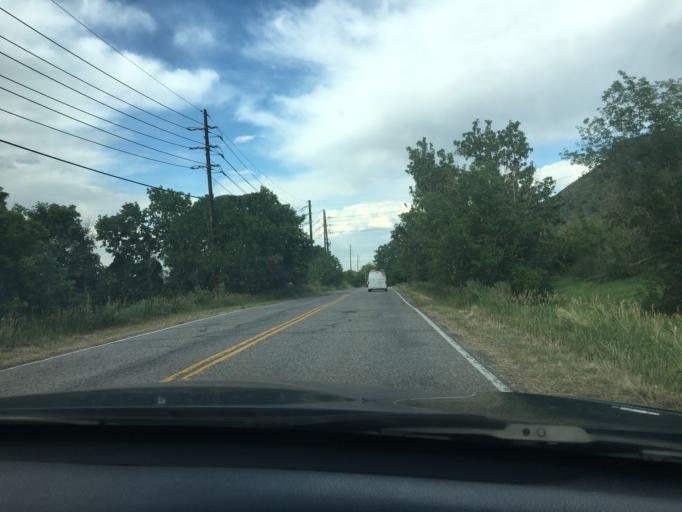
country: US
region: Colorado
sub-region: Jefferson County
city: Golden
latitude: 39.7645
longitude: -105.1976
